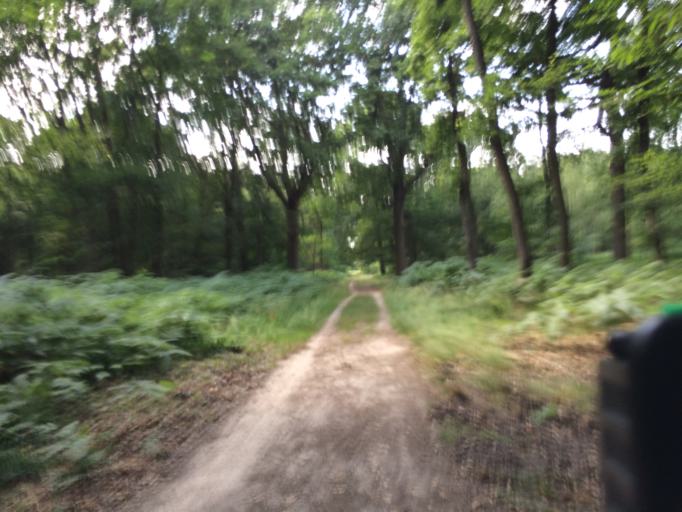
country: FR
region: Ile-de-France
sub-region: Departement de l'Essonne
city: Soisy-sur-Seine
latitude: 48.6668
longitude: 2.4471
